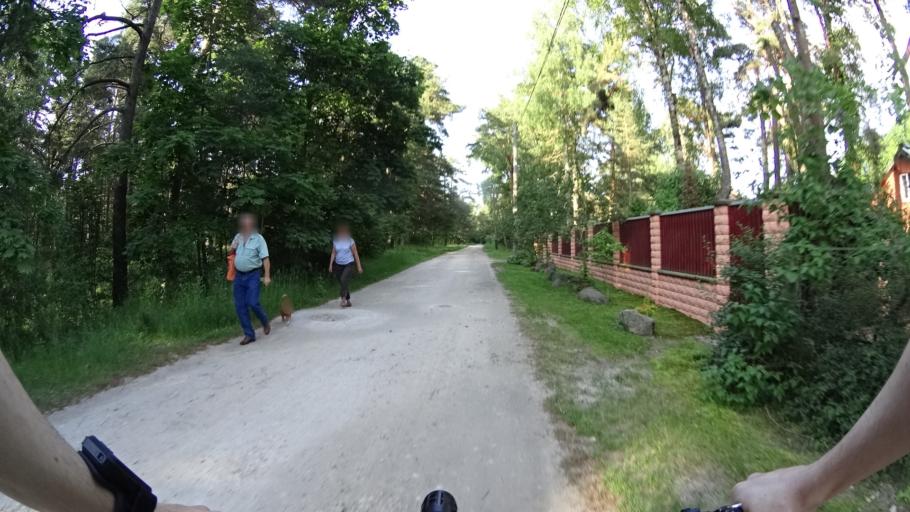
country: LV
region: Riga
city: Bolderaja
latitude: 57.0797
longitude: 24.1109
